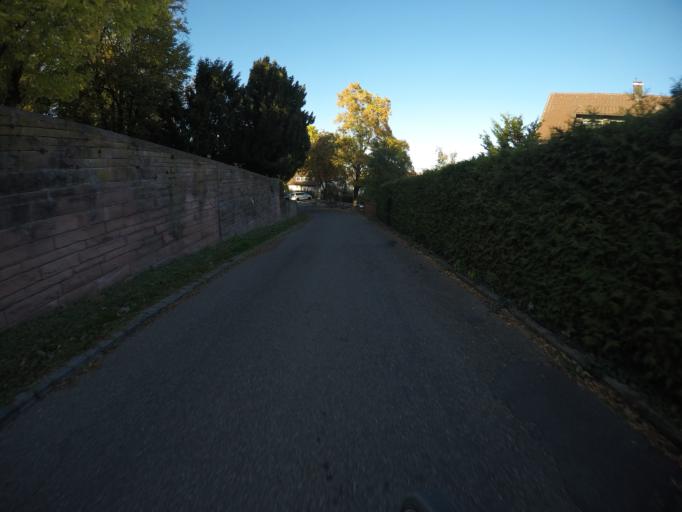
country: DE
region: Baden-Wuerttemberg
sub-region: Regierungsbezirk Stuttgart
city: Stuttgart-Ost
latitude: 48.7694
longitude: 9.2420
